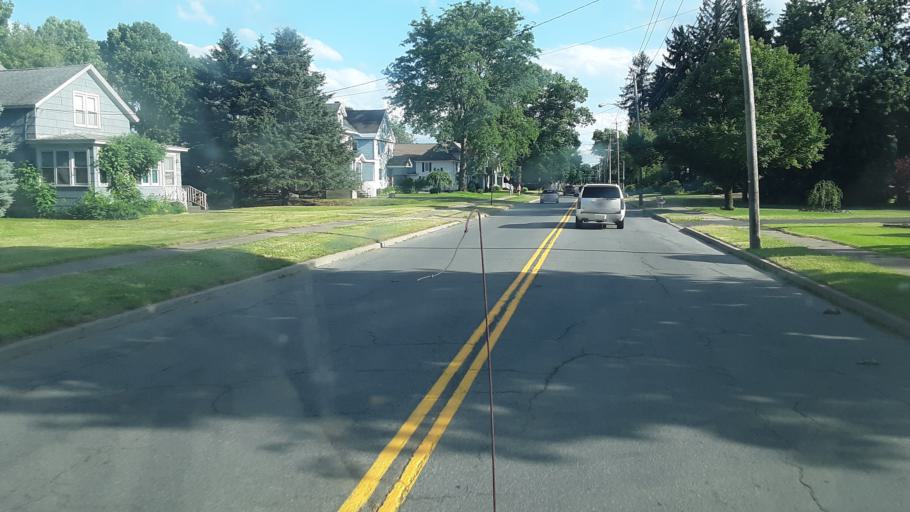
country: US
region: New York
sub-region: Oneida County
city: Rome
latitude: 43.2319
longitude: -75.4553
